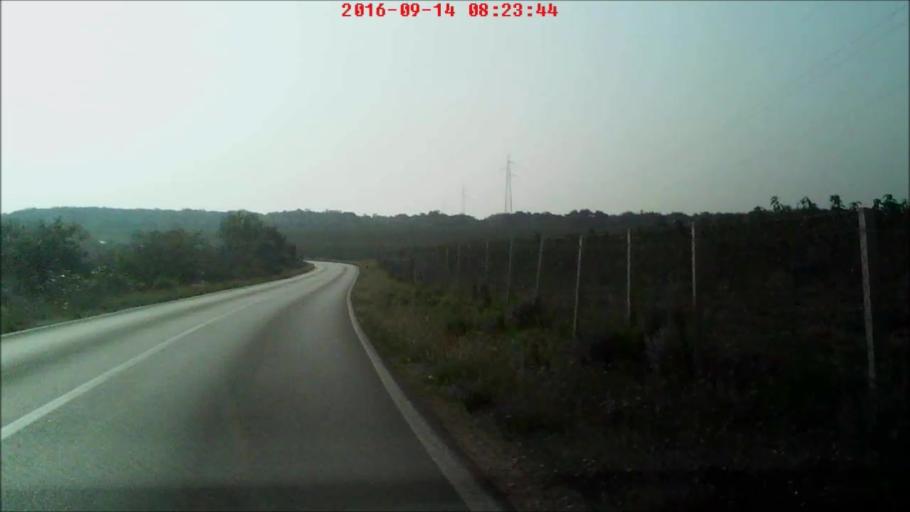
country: HR
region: Zadarska
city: Vrsi
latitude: 44.2105
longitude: 15.2349
